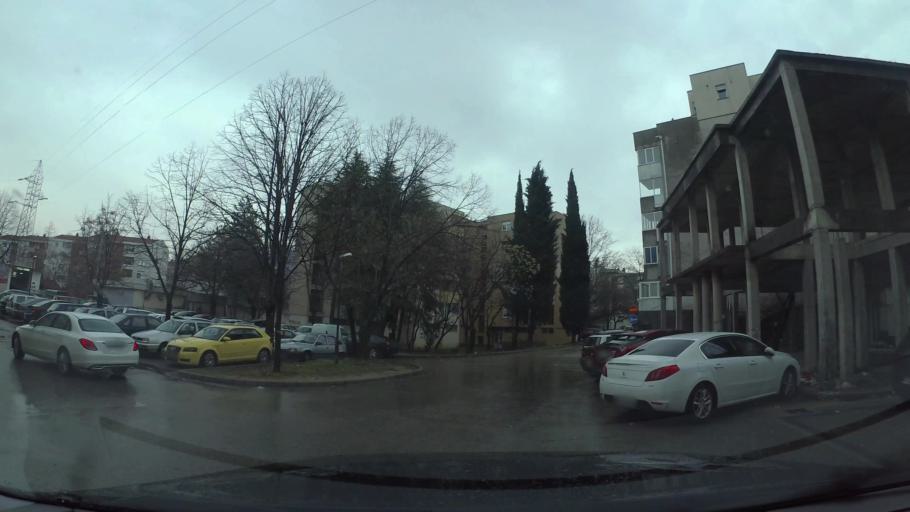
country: BA
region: Federation of Bosnia and Herzegovina
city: Cim
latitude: 43.3505
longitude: 17.7949
